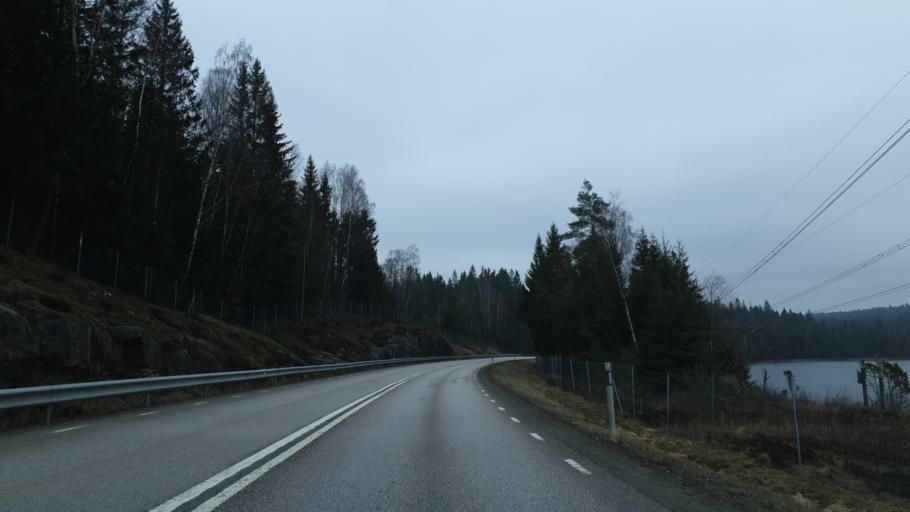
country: SE
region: Vaestra Goetaland
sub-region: Harryda Kommun
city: Hindas
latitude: 57.6408
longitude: 12.4054
